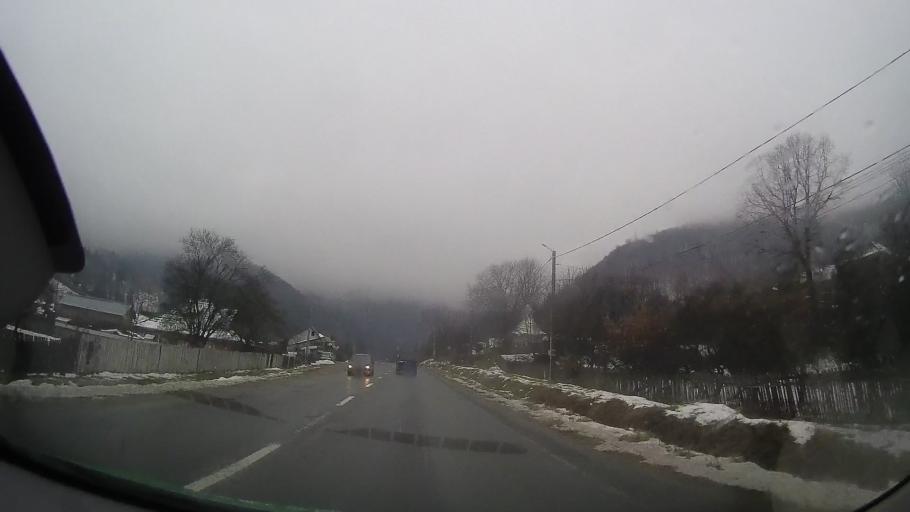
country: RO
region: Neamt
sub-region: Comuna Pangarati
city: Stejaru
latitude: 46.8971
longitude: 26.1708
